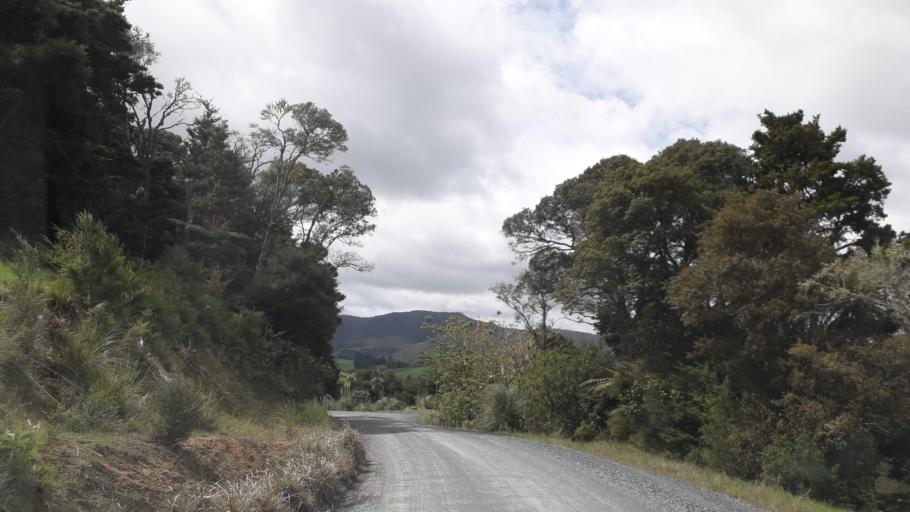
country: NZ
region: Northland
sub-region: Far North District
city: Kaitaia
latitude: -35.1707
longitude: 173.3416
